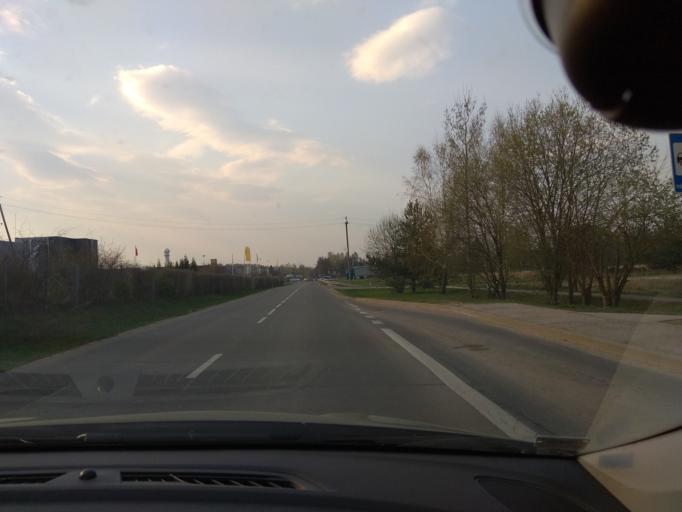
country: LT
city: Grigiskes
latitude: 54.6219
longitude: 25.1129
